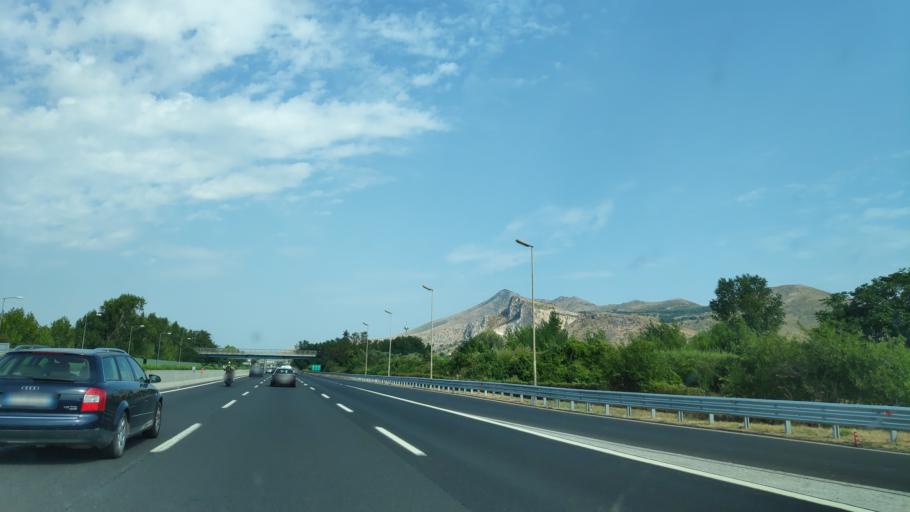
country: IT
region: Campania
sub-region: Provincia di Caserta
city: Casapulla
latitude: 41.0773
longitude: 14.2974
